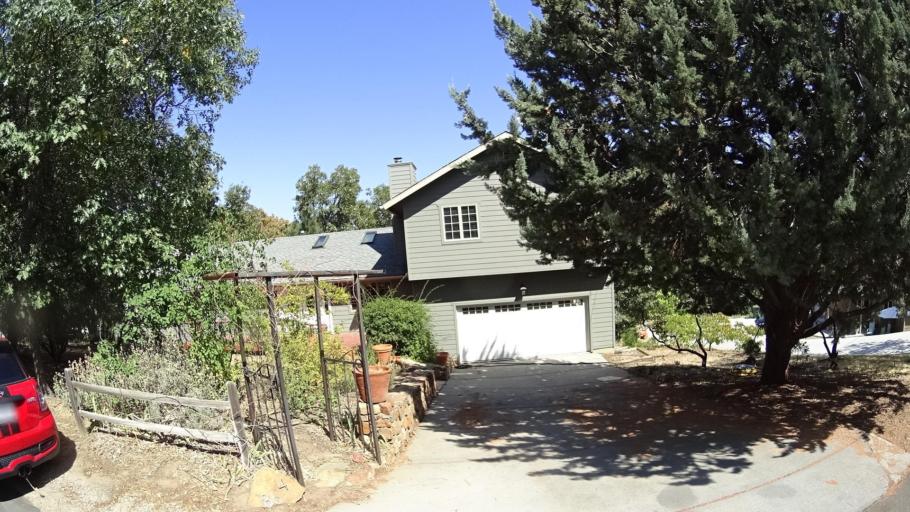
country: US
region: California
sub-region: San Diego County
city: Julian
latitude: 33.0648
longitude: -116.5784
